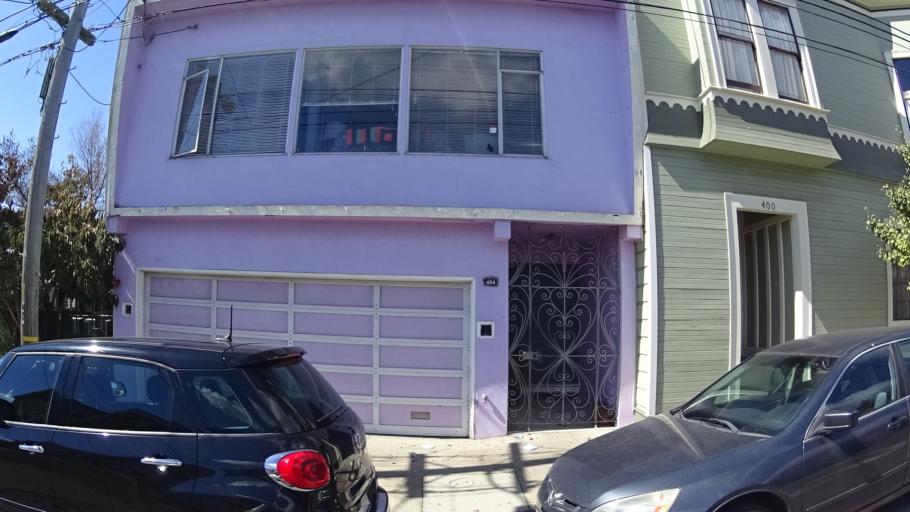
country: US
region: California
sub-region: San Francisco County
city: San Francisco
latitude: 37.7382
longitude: -122.4128
